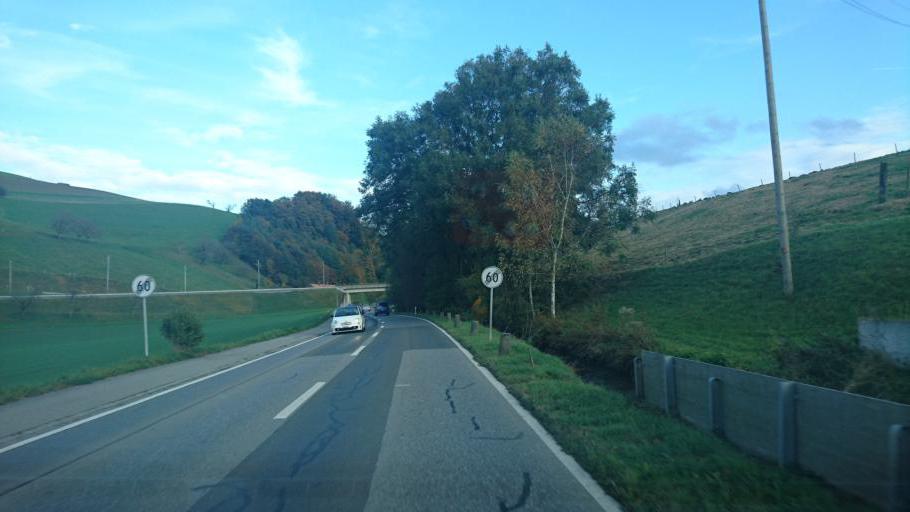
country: CH
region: Bern
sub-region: Bern-Mittelland District
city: Biglen
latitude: 46.9321
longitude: 7.6150
